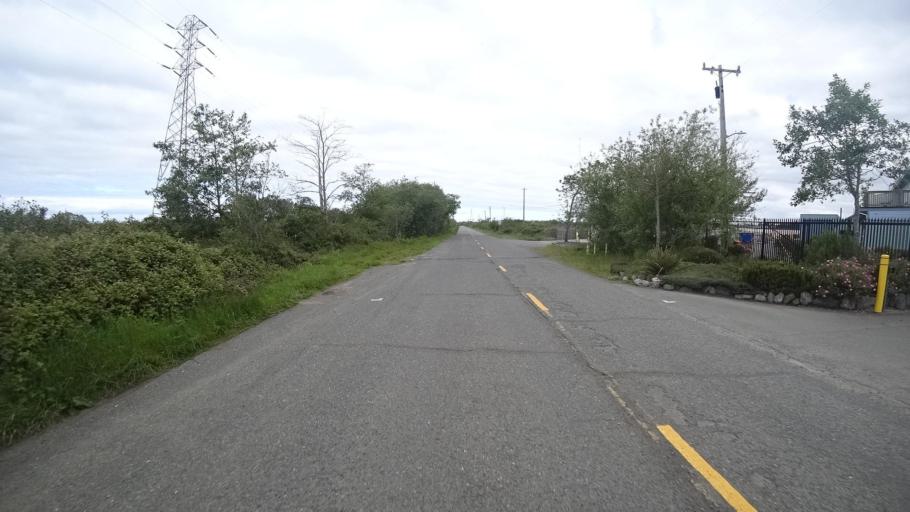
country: US
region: California
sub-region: Humboldt County
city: Arcata
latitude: 40.8520
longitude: -124.0838
